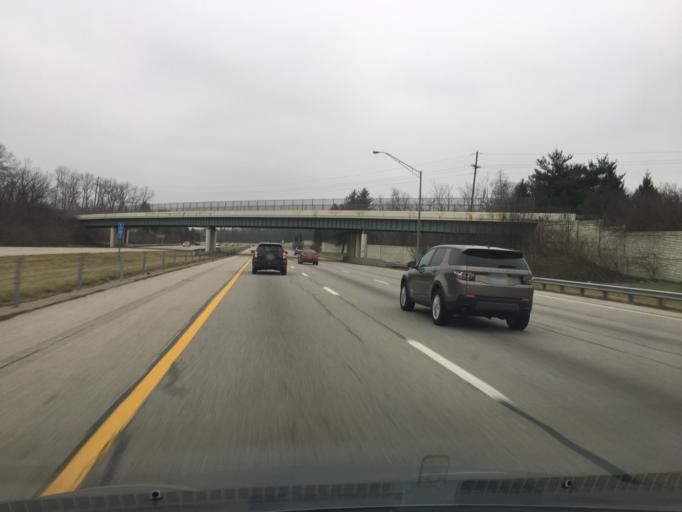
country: US
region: Ohio
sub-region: Hamilton County
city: Sixteen Mile Stand
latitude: 39.2572
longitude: -84.3327
